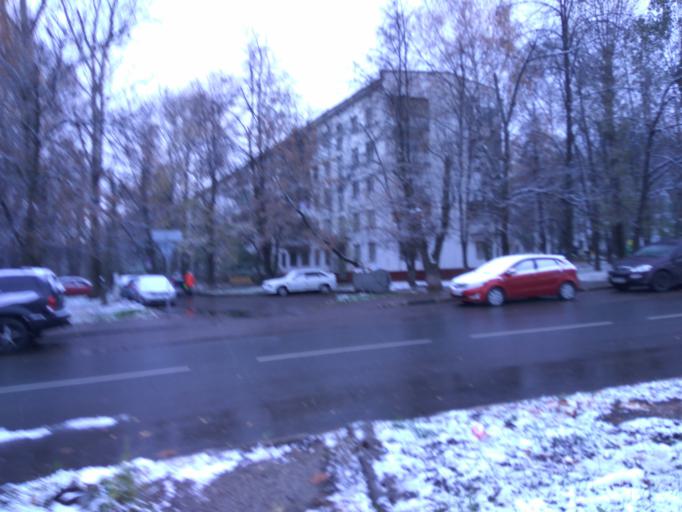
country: RU
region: Moscow
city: Orekhovo-Borisovo Severnoye
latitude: 55.6300
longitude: 37.6722
